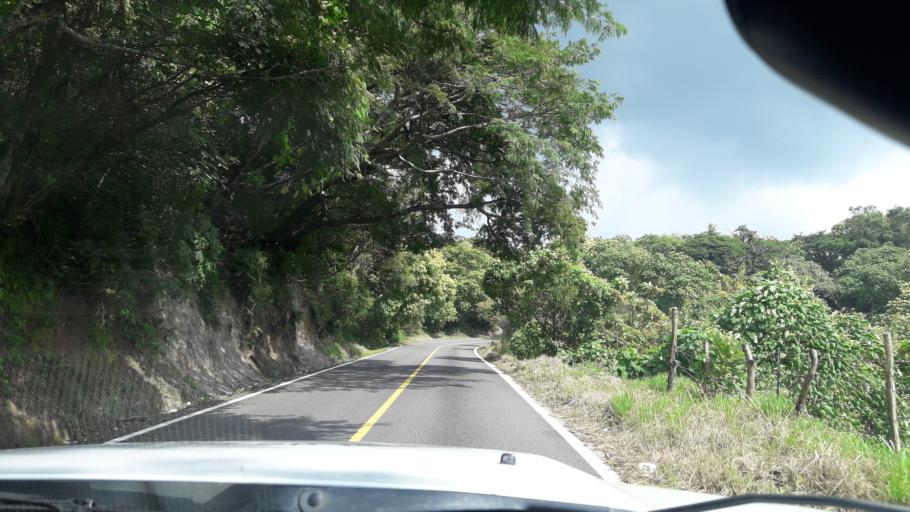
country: MX
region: Colima
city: Suchitlan
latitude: 19.4355
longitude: -103.7051
